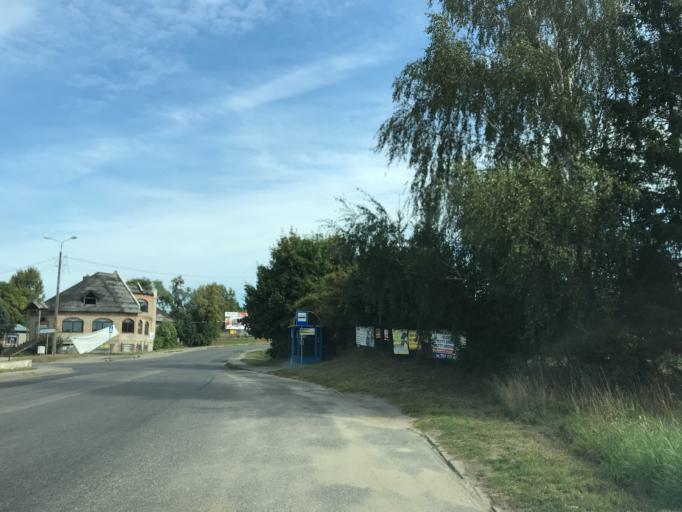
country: PL
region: Pomeranian Voivodeship
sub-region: Powiat pucki
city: Krokowa
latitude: 54.7819
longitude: 18.1701
